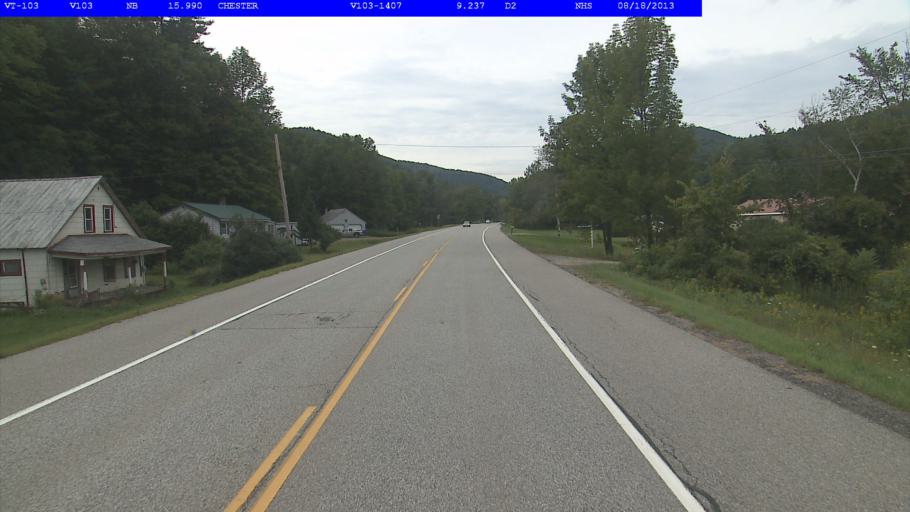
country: US
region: Vermont
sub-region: Windsor County
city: Chester
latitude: 43.3430
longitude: -72.6215
